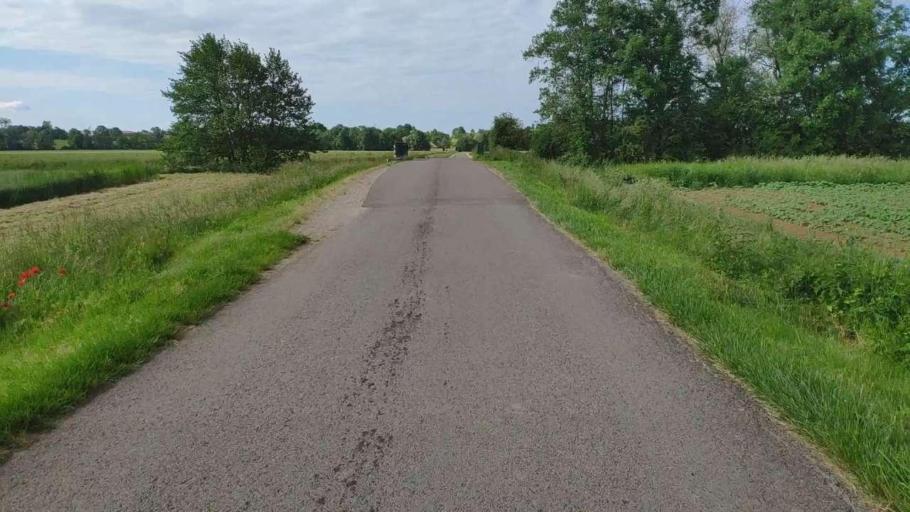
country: FR
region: Franche-Comte
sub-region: Departement du Jura
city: Bletterans
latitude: 46.7237
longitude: 5.4625
